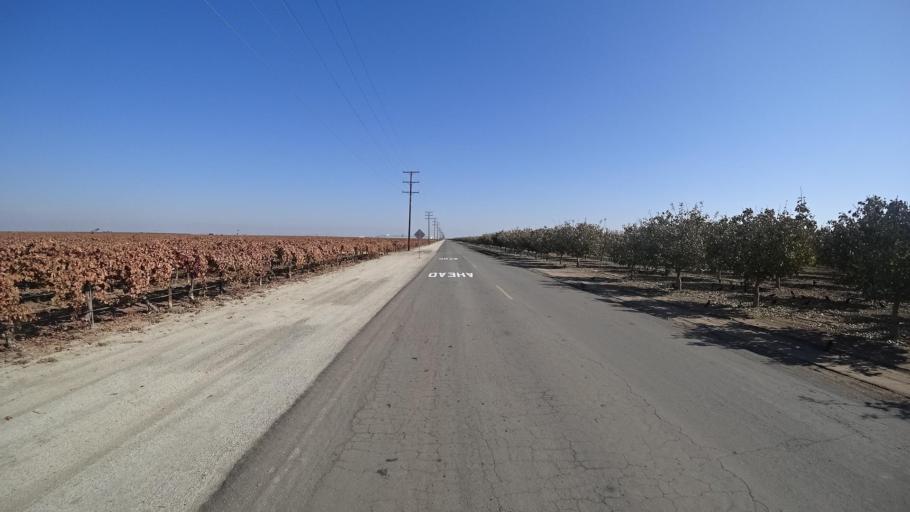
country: US
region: California
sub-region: Kern County
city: McFarland
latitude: 35.7034
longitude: -119.2211
